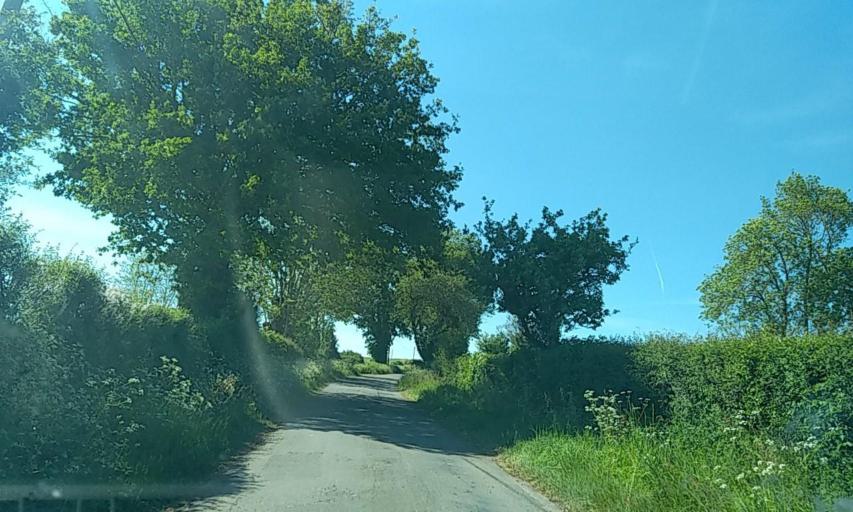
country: FR
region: Poitou-Charentes
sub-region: Departement des Deux-Sevres
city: Boisme
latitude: 46.7744
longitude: -0.4134
